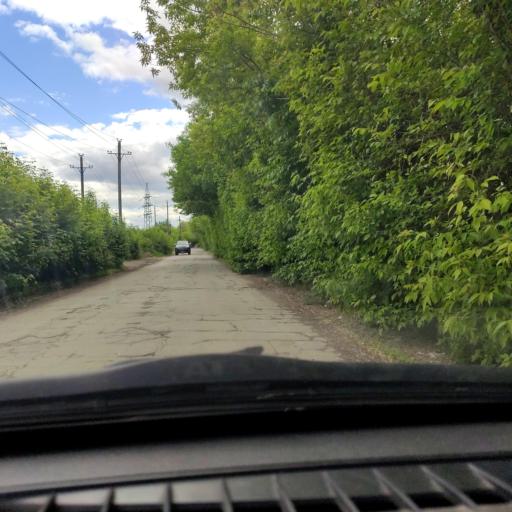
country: RU
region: Samara
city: Tol'yatti
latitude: 53.5230
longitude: 49.4555
